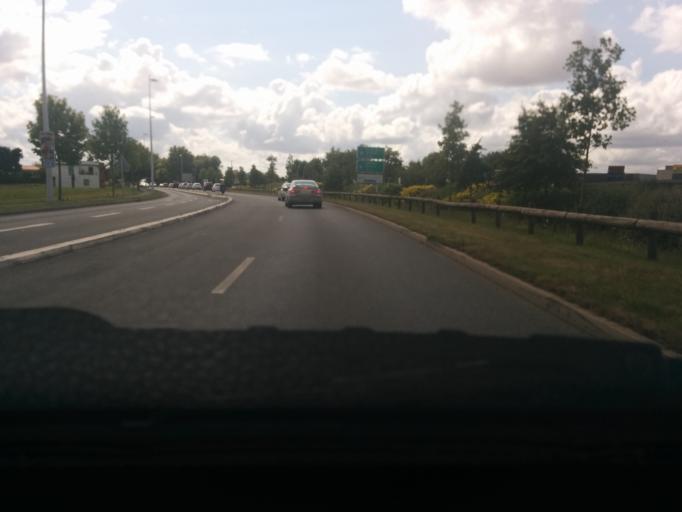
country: FR
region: Pays de la Loire
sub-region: Departement de la Vendee
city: Les Herbiers
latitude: 46.8777
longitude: -1.0190
